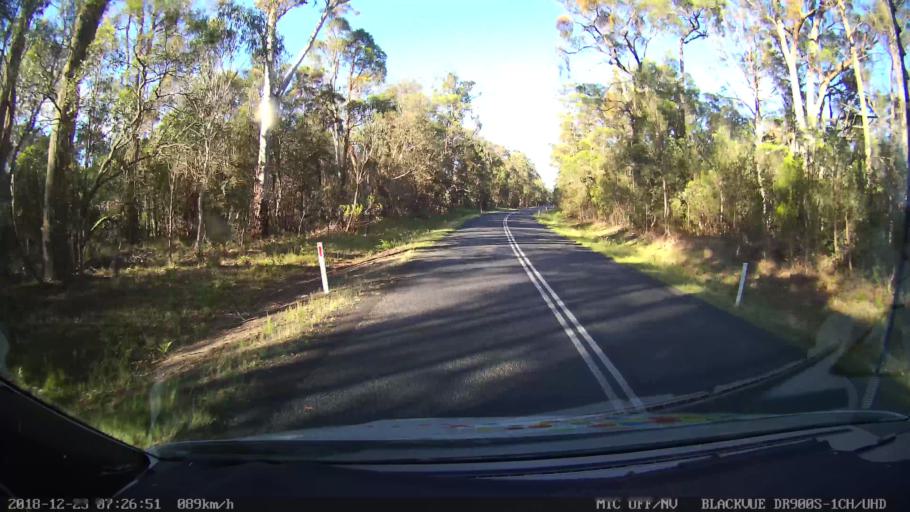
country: AU
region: New South Wales
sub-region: Armidale Dumaresq
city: Enmore
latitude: -30.4943
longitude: 152.1932
